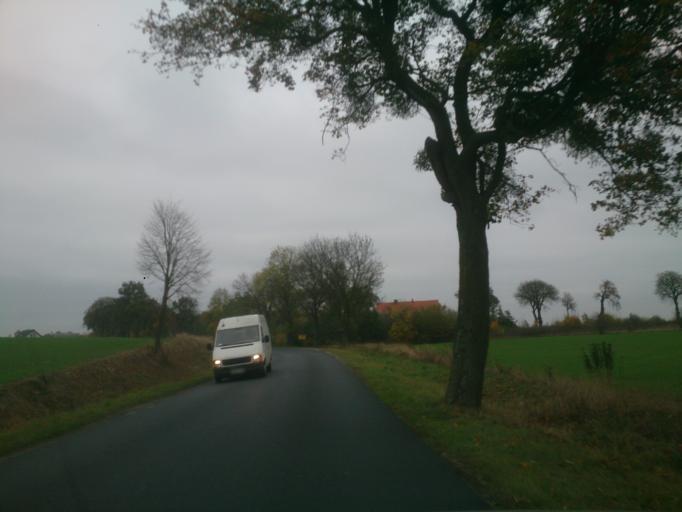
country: PL
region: Kujawsko-Pomorskie
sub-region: Powiat brodnicki
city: Brodnica
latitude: 53.2962
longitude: 19.3972
